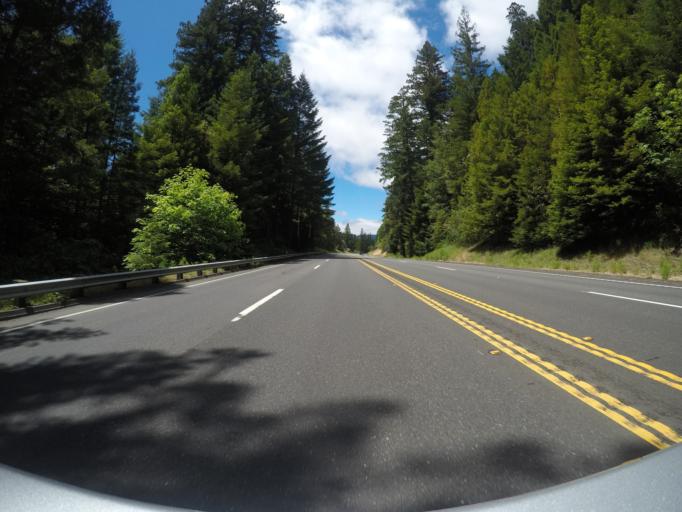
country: US
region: California
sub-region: Humboldt County
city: Redway
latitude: 40.2724
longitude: -123.8770
